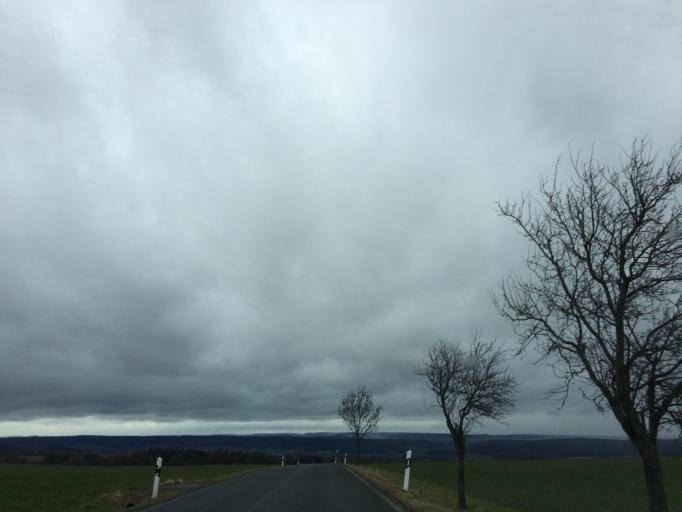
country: DE
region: Thuringia
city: Quaschwitz
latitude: 50.6850
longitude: 11.6995
